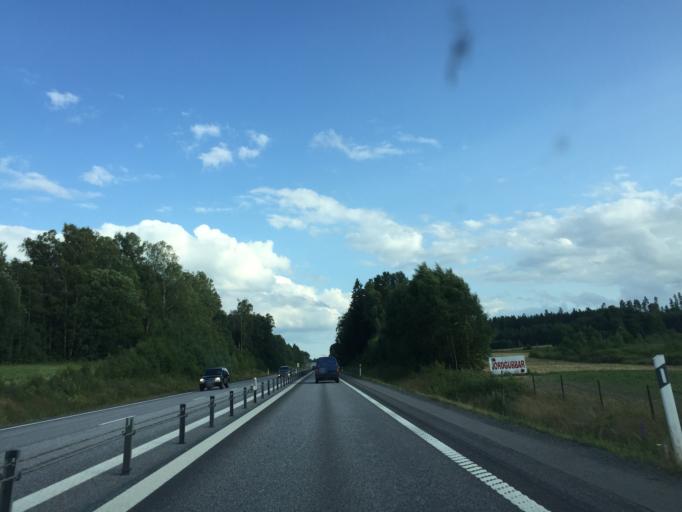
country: SE
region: OEstergoetland
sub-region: Motala Kommun
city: Motala
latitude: 58.6167
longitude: 14.9805
